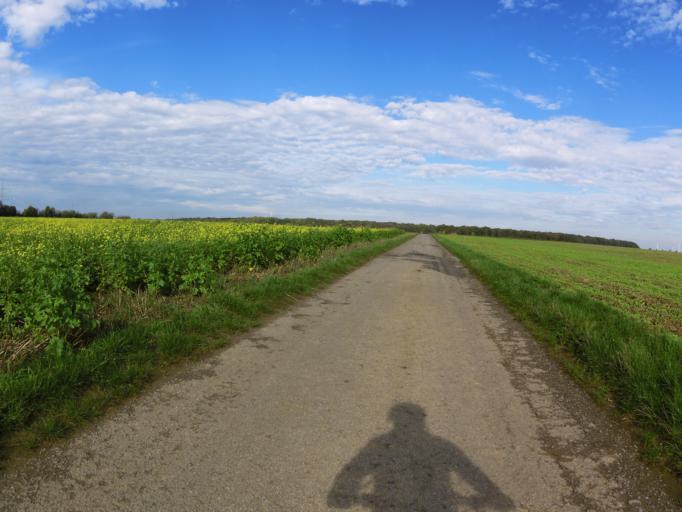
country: DE
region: Bavaria
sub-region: Regierungsbezirk Unterfranken
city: Sommerhausen
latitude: 49.7179
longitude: 10.0619
